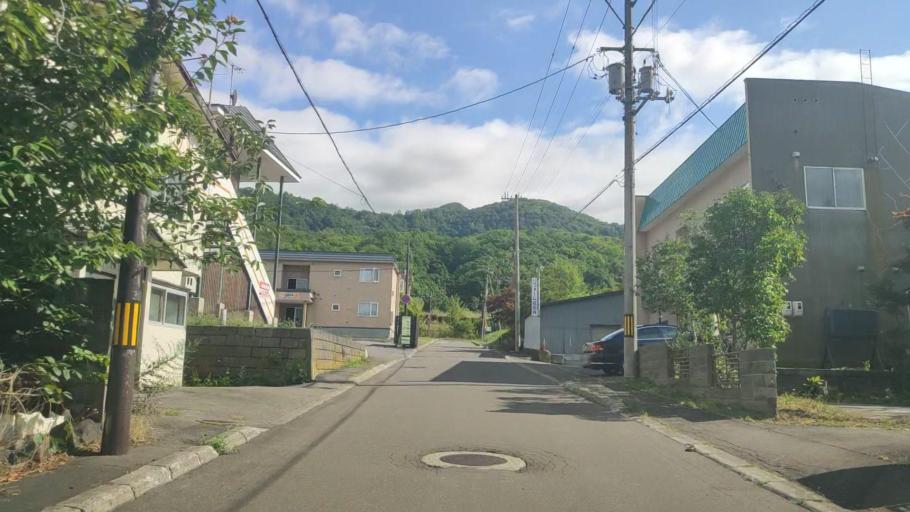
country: JP
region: Hokkaido
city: Date
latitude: 42.5625
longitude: 140.8255
